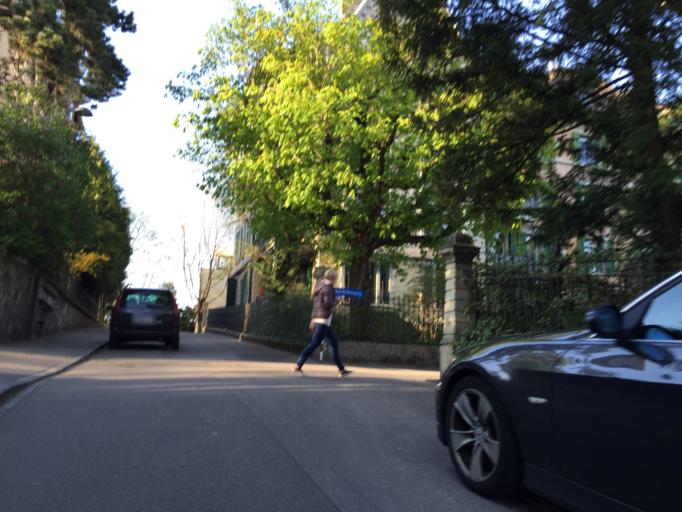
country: CH
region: Bern
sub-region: Bern-Mittelland District
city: Bern
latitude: 46.9504
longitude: 7.4336
